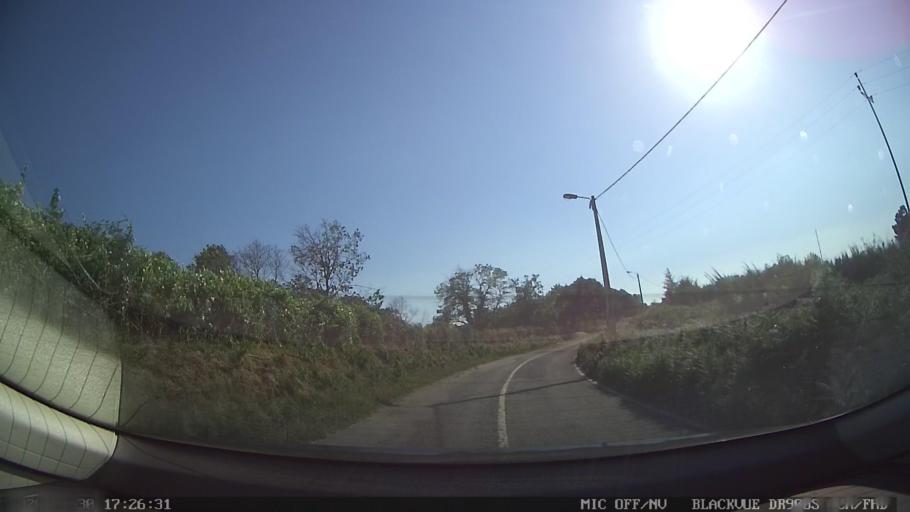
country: PT
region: Vila Real
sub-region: Murca
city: Murca
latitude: 41.3164
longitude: -7.4648
